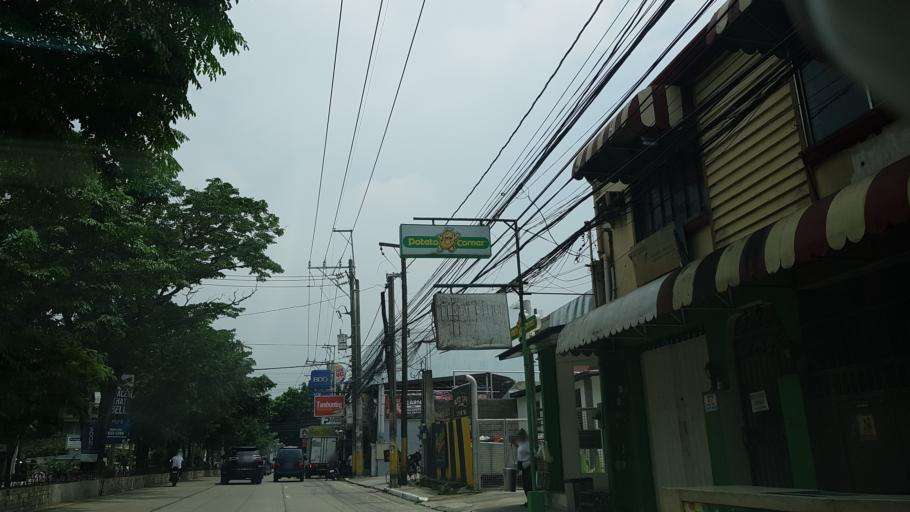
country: PH
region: Metro Manila
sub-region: Makati City
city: Makati City
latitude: 14.5290
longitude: 121.0417
